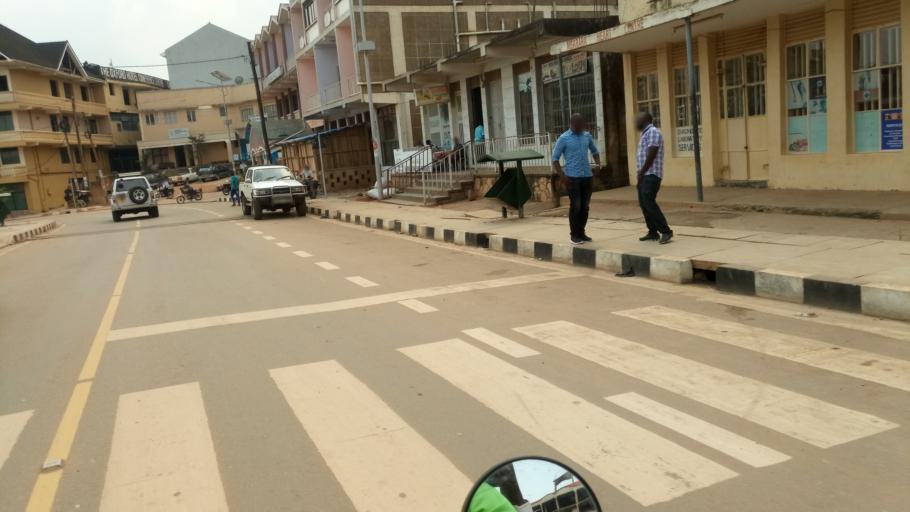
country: UG
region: Western Region
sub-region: Mbarara District
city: Mbarara
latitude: -0.6084
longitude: 30.6625
